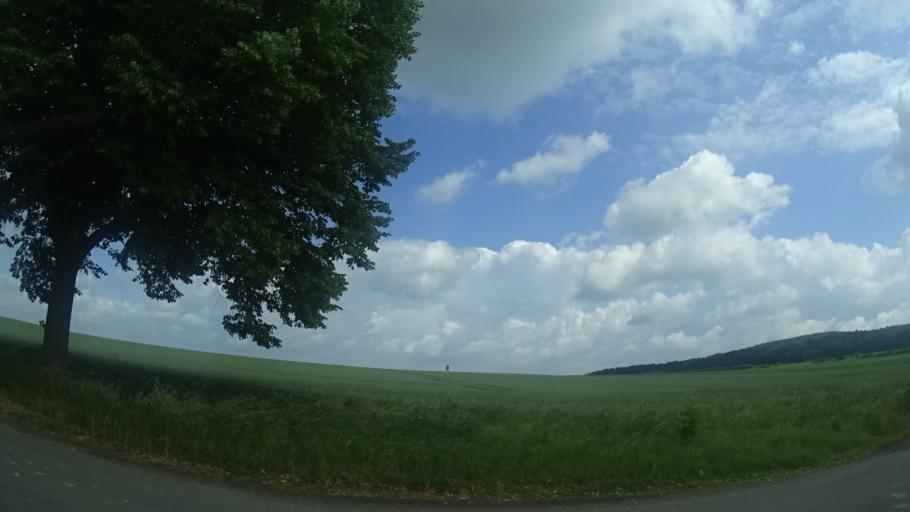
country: DE
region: Lower Saxony
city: Wennigsen
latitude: 52.2423
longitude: 9.6421
